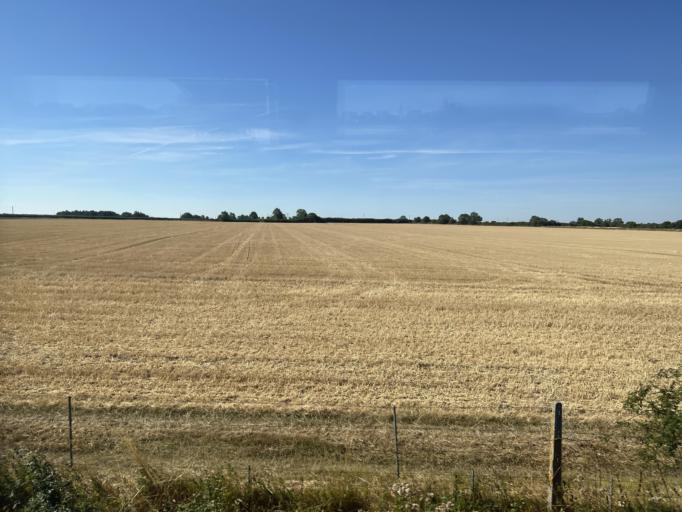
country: GB
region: England
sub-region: Lincolnshire
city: Heckington
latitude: 52.9864
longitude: -0.3412
